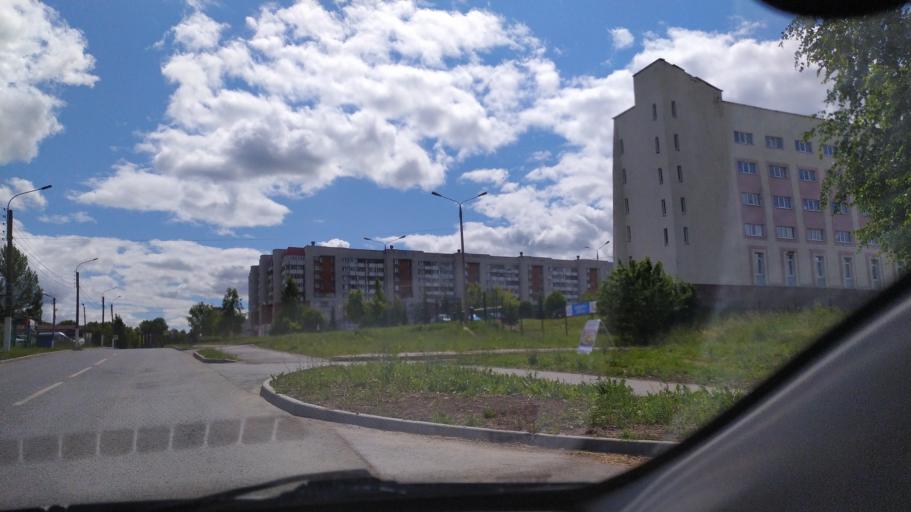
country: RU
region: Chuvashia
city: Novyye Lapsary
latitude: 56.1231
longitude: 47.1881
